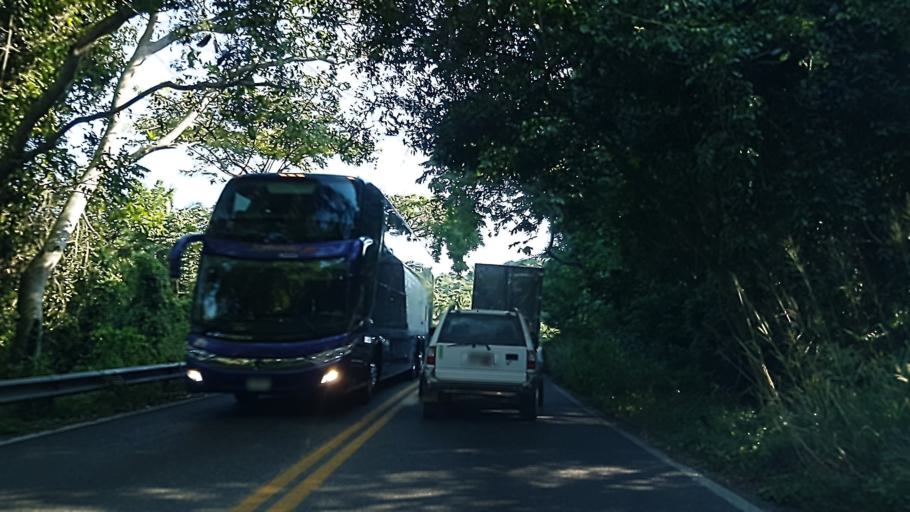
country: MX
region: Nayarit
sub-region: Bahia de Banderas
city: Lo de Marcos
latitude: 20.8819
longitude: -105.4199
